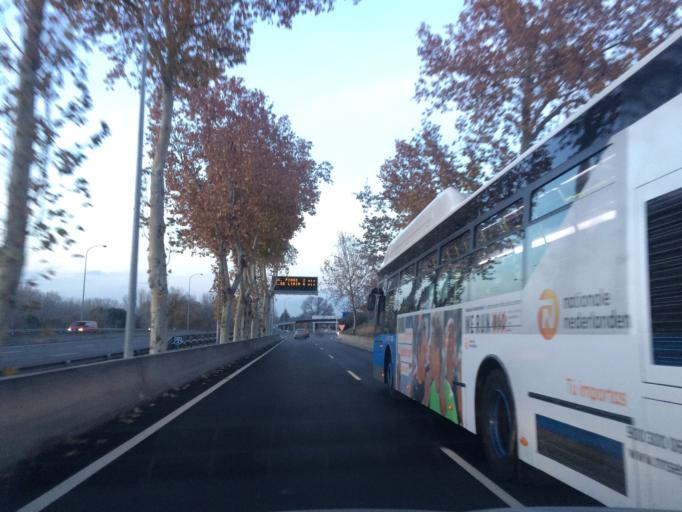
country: ES
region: Madrid
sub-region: Provincia de Madrid
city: Moncloa-Aravaca
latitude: 40.4572
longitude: -3.7442
